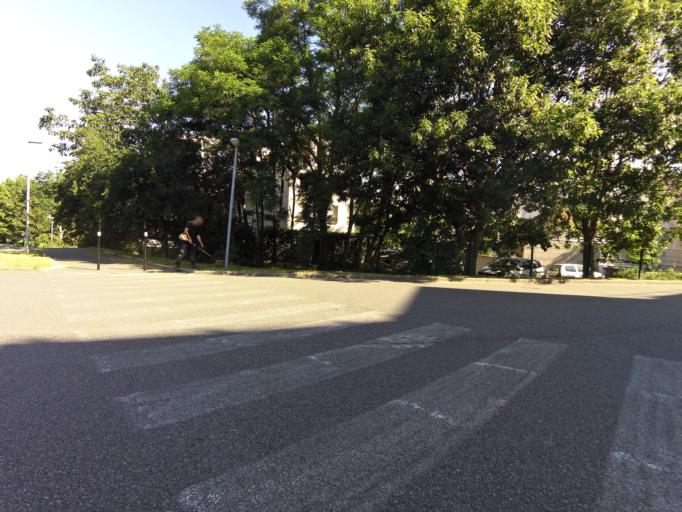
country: FR
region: Pays de la Loire
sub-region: Departement de la Loire-Atlantique
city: Saint-Herblain
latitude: 47.2274
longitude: -1.6114
